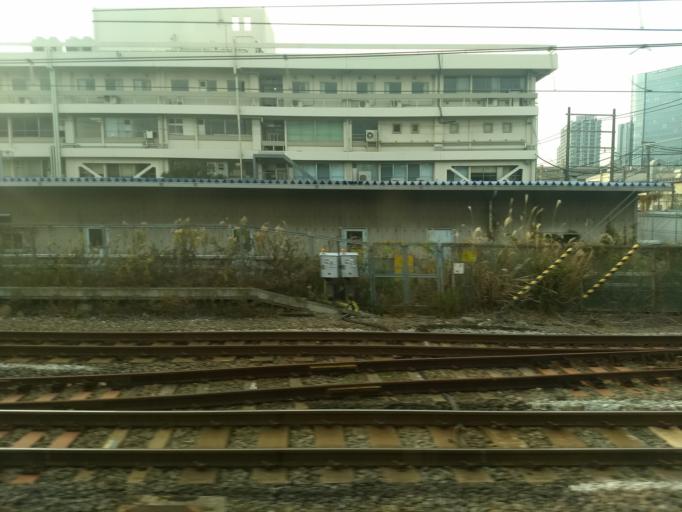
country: JP
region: Tokyo
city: Tokyo
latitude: 35.6117
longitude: 139.7356
